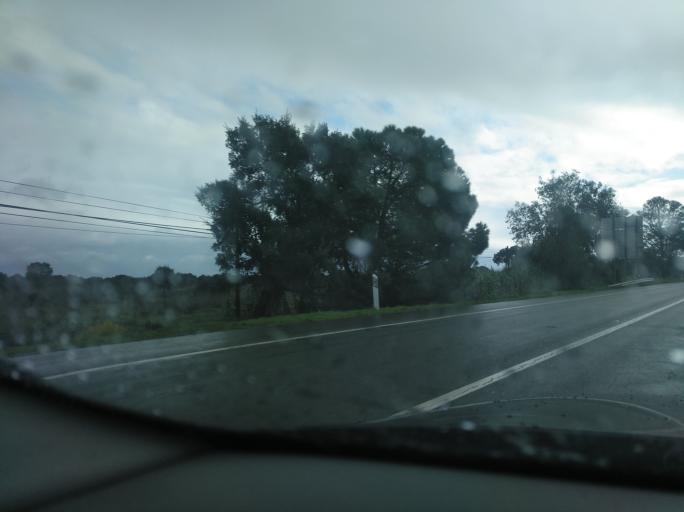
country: PT
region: Setubal
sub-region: Grandola
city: Grandola
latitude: 38.1028
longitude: -8.4184
